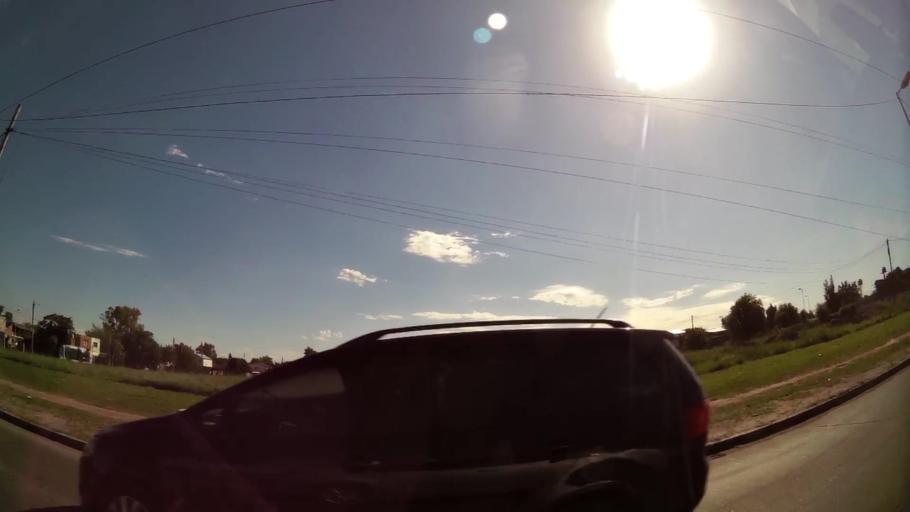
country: AR
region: Buenos Aires
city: Santa Catalina - Dique Lujan
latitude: -34.4646
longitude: -58.7135
